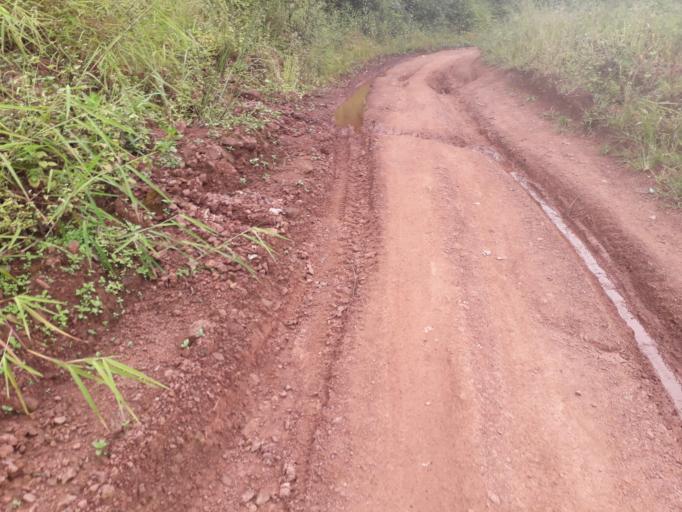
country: CN
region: Yunnan
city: Menglie
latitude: 22.2166
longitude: 101.6539
